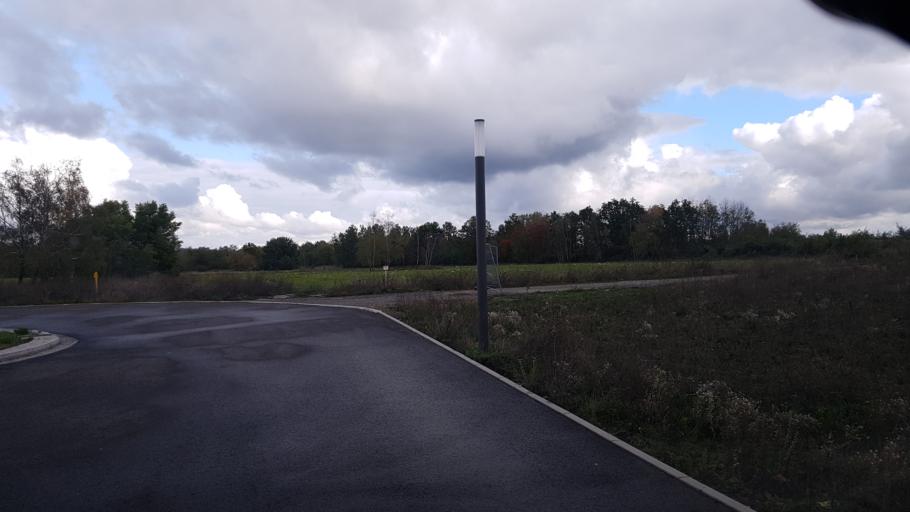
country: DE
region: Brandenburg
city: Grossraschen
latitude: 51.5750
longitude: 14.0156
